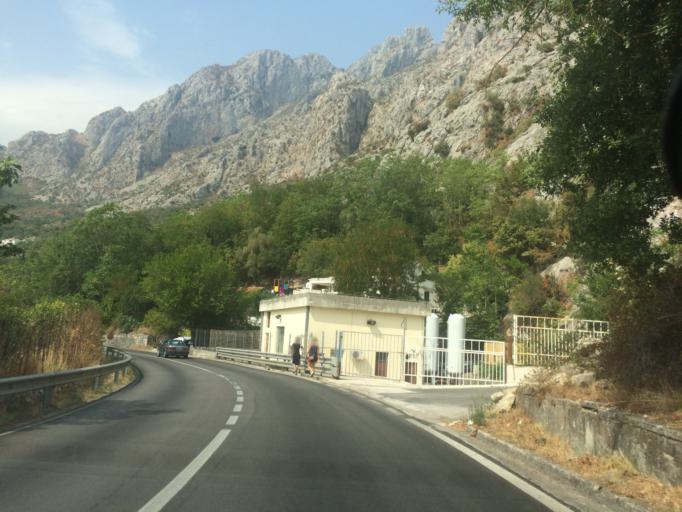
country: ME
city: Dobrota
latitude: 42.4879
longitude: 18.7654
